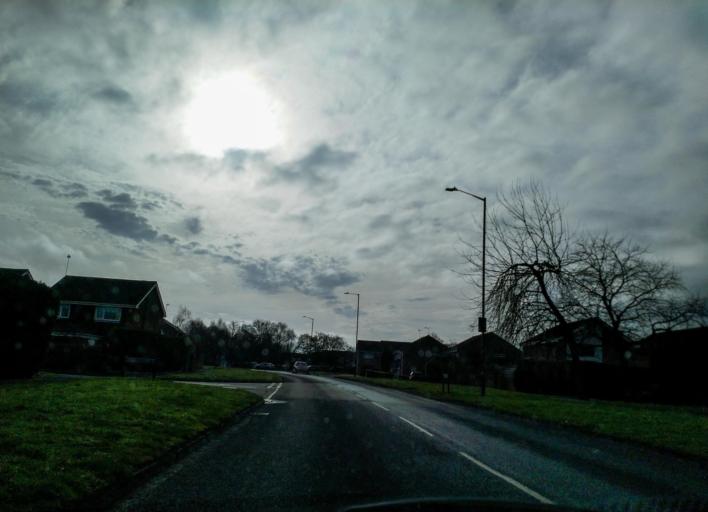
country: GB
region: England
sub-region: Warwickshire
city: Warwick
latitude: 52.2959
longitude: -1.5785
